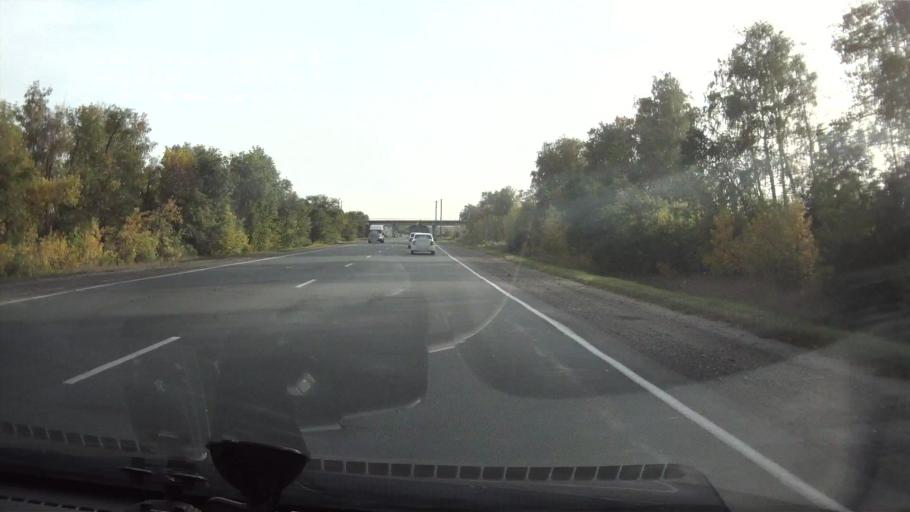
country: RU
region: Saratov
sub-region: Saratovskiy Rayon
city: Saratov
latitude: 51.6988
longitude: 46.0099
